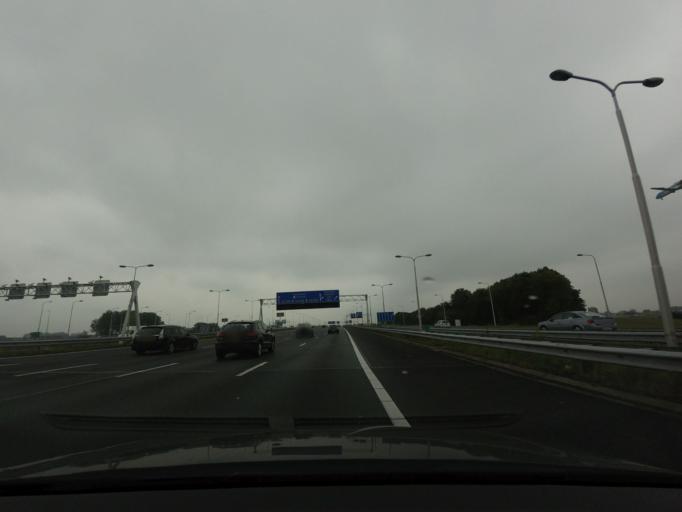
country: NL
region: North Holland
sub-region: Gemeente Haarlemmermeer
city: Hoofddorp
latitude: 52.2849
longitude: 4.7224
